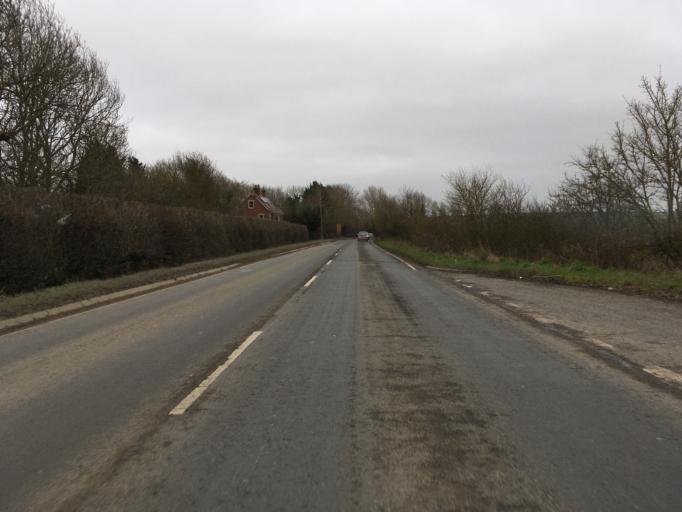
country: GB
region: England
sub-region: Oxfordshire
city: Wantage
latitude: 51.6004
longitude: -1.4697
